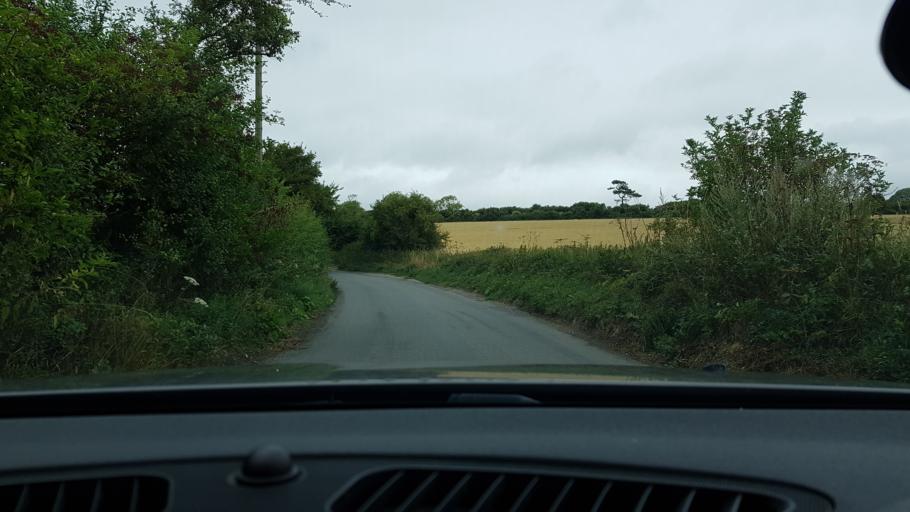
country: GB
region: England
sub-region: Wiltshire
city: Shalbourne
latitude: 51.3718
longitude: -1.5320
